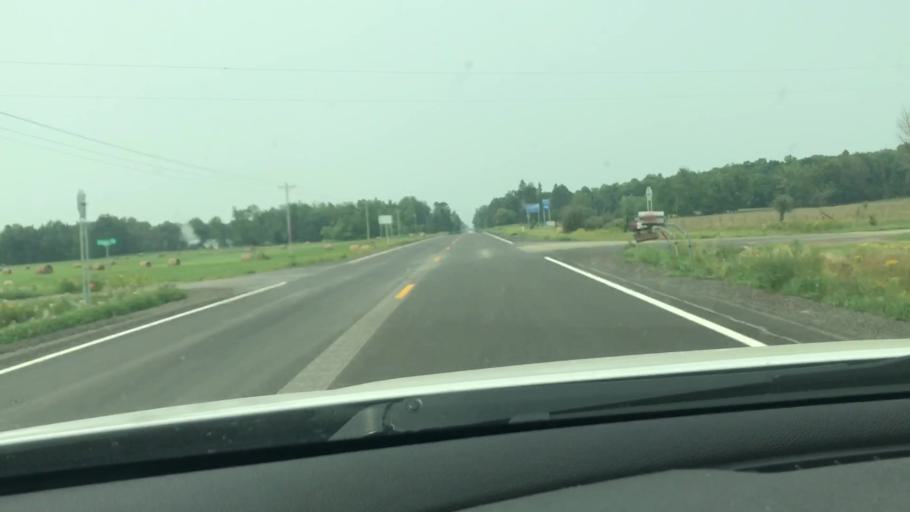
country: US
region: Minnesota
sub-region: Itasca County
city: Cohasset
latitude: 47.3548
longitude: -93.8487
